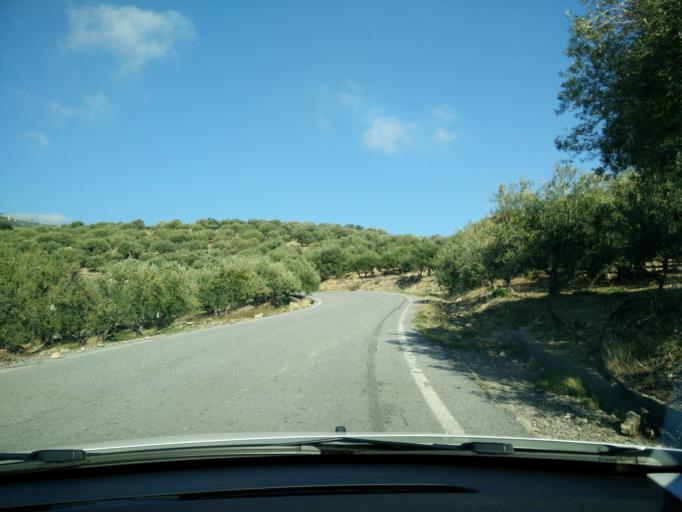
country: GR
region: Crete
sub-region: Nomos Lasithiou
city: Gra Liyia
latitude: 34.9988
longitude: 25.5142
